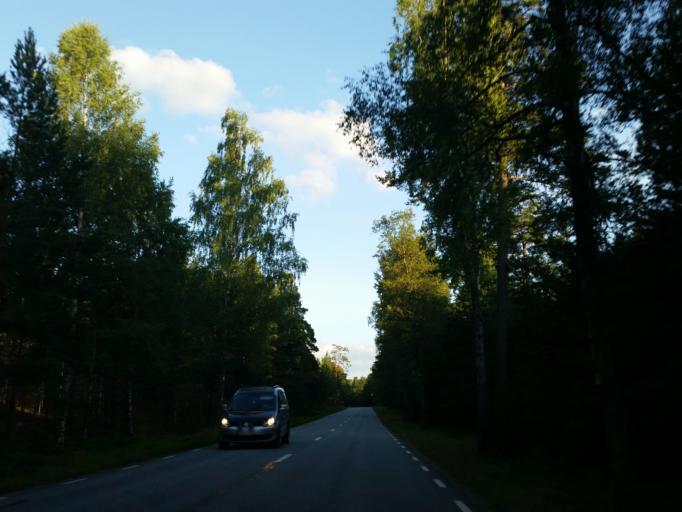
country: SE
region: Stockholm
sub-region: Sodertalje Kommun
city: Soedertaelje
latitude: 59.2380
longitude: 17.5445
